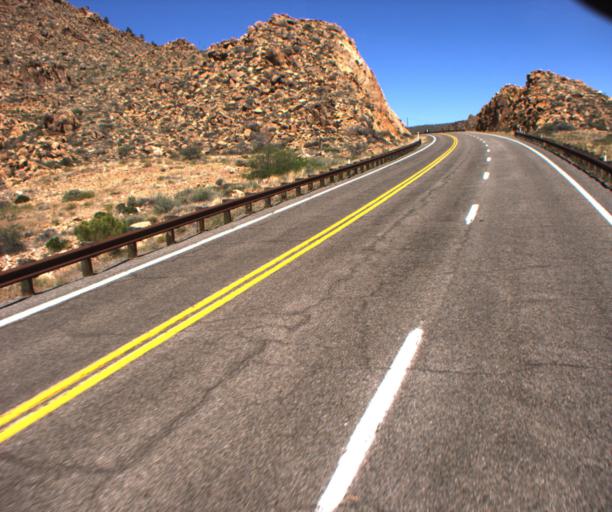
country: US
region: Arizona
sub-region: Mohave County
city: Peach Springs
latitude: 35.4113
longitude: -113.6474
